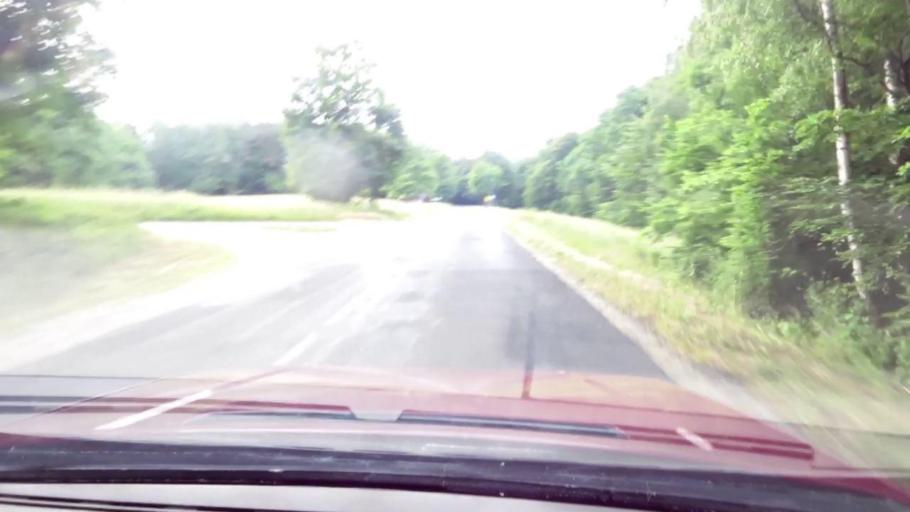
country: PL
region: Pomeranian Voivodeship
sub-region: Powiat bytowski
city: Trzebielino
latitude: 54.2671
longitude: 17.0042
